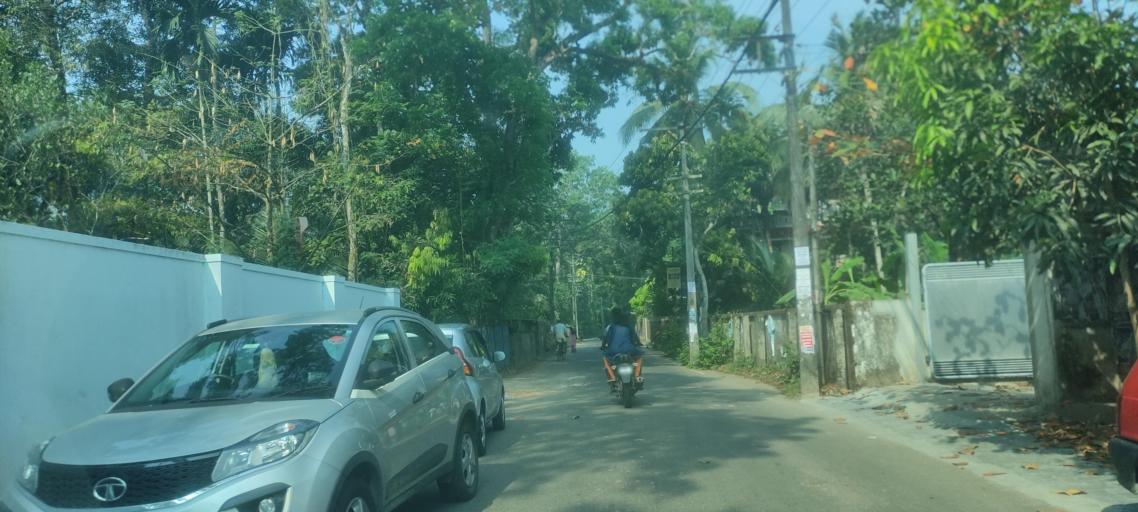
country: IN
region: Kerala
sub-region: Alappuzha
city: Kutiatodu
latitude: 9.7686
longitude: 76.3163
